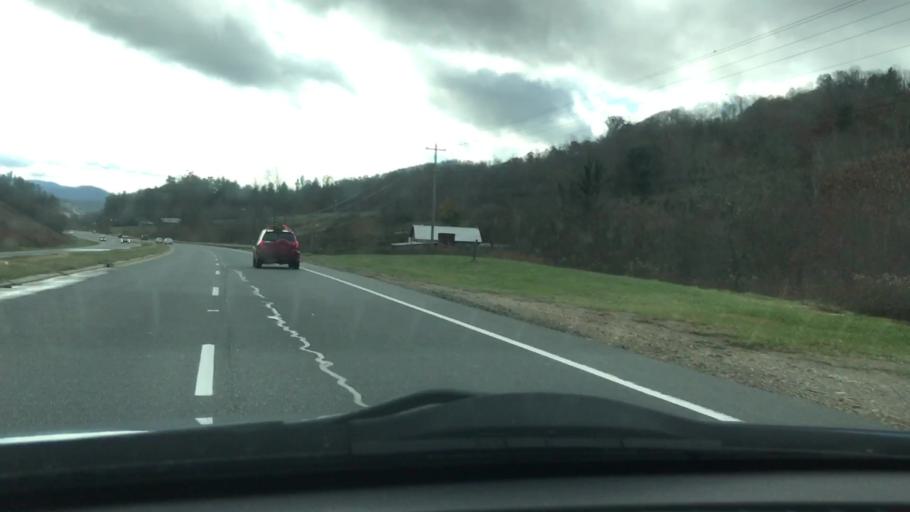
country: US
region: North Carolina
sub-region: Madison County
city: Mars Hill
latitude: 35.8903
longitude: -82.4760
